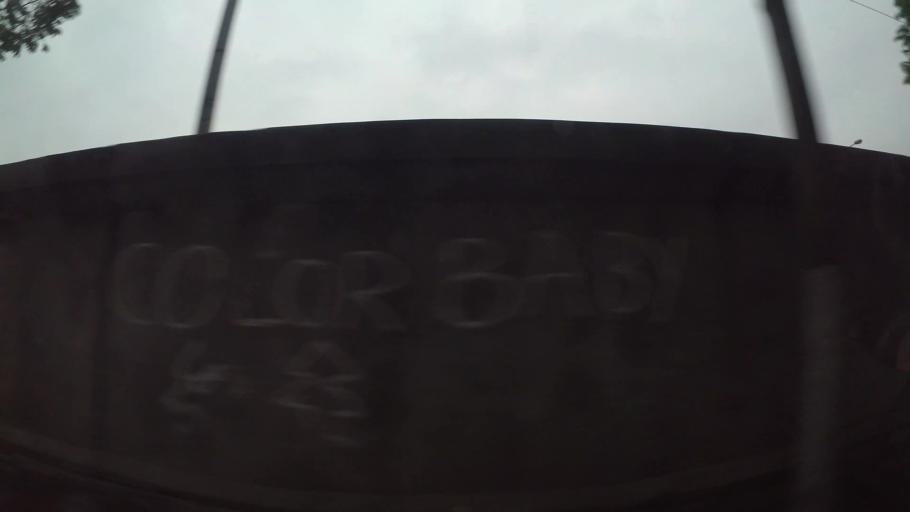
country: VN
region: Ha Noi
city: Hai BaTrung
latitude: 21.0093
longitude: 105.8656
